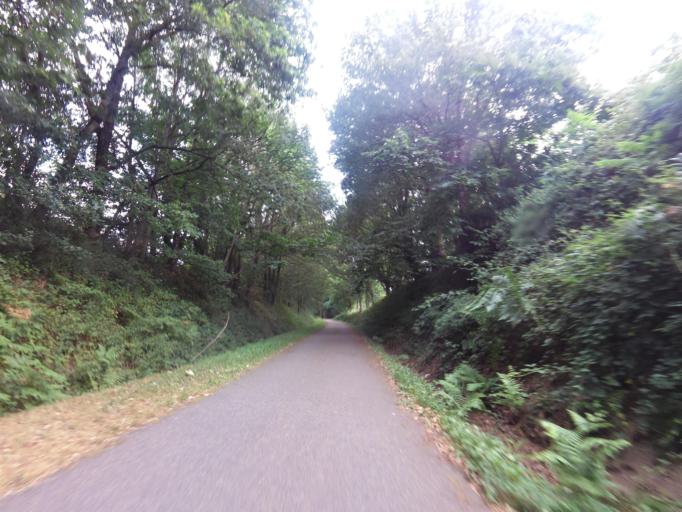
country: FR
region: Brittany
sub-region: Departement du Morbihan
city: Malestroit
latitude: 47.8232
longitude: -2.4198
